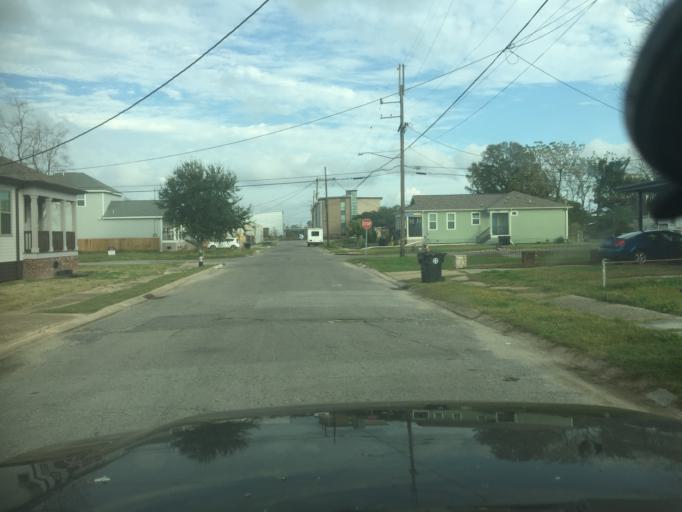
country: US
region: Louisiana
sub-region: Orleans Parish
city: New Orleans
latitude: 29.9966
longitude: -90.0812
